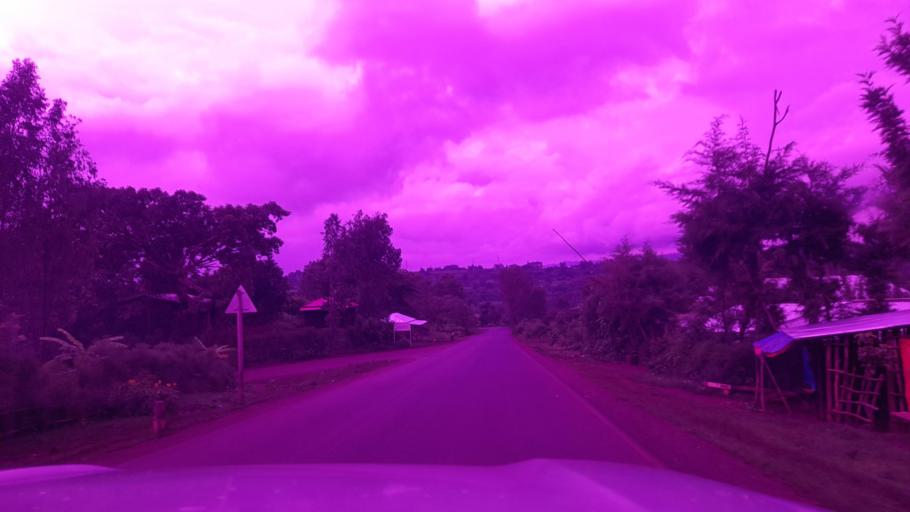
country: ET
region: Oromiya
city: Jima
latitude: 7.9173
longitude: 37.4040
